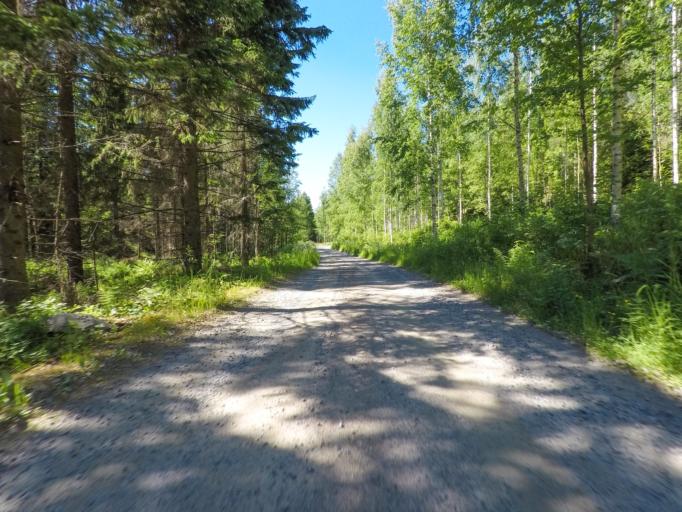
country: FI
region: Northern Savo
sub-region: Varkaus
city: Kangaslampi
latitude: 62.1739
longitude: 28.2410
